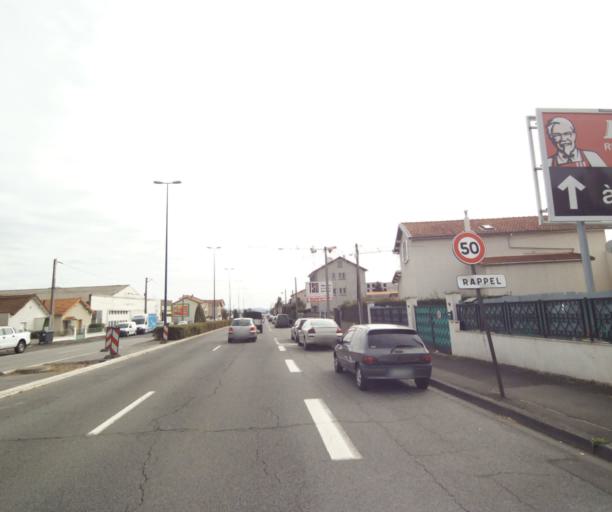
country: FR
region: Auvergne
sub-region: Departement du Puy-de-Dome
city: Aubiere
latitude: 45.7713
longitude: 3.1221
